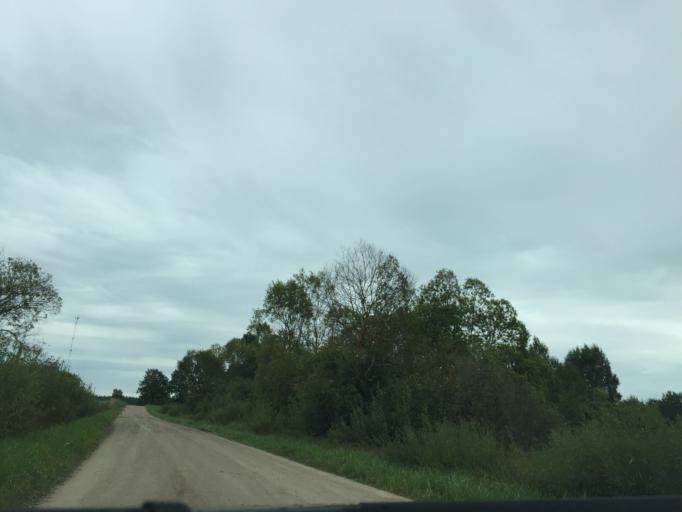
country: LV
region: Preilu Rajons
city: Jaunaglona
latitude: 56.2692
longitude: 27.0760
